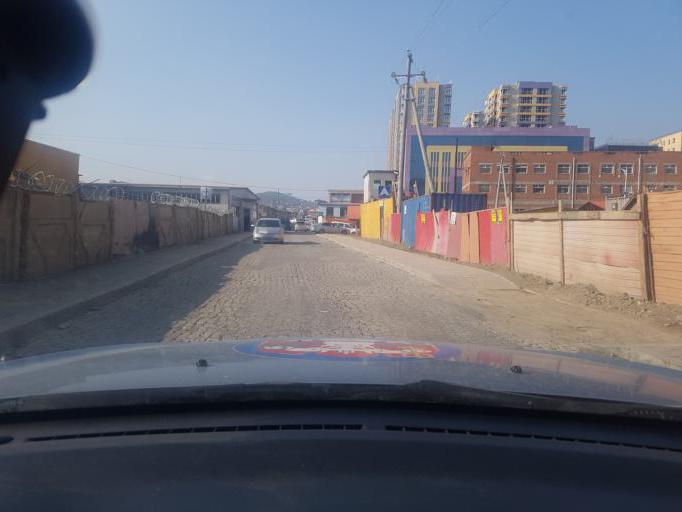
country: MN
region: Ulaanbaatar
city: Ulaanbaatar
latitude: 47.9227
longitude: 106.9667
